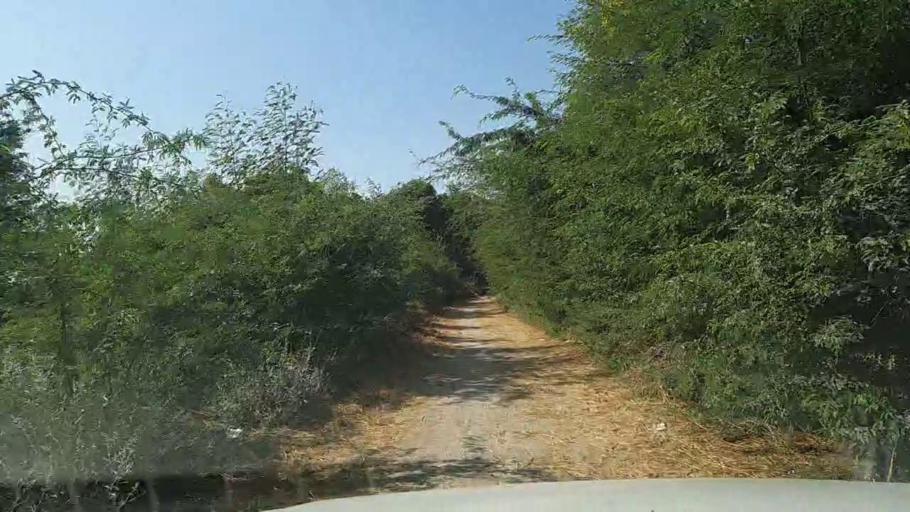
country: PK
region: Sindh
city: Mirpur Batoro
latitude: 24.6900
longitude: 68.1773
